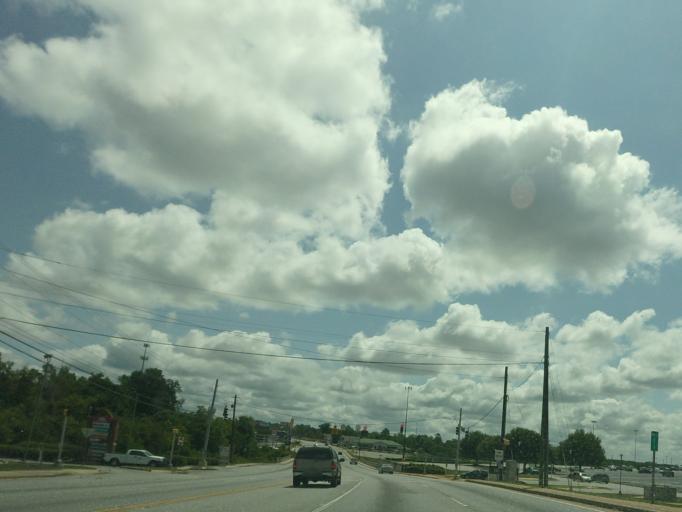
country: US
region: Georgia
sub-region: Bibb County
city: Macon
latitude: 32.8205
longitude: -83.6941
